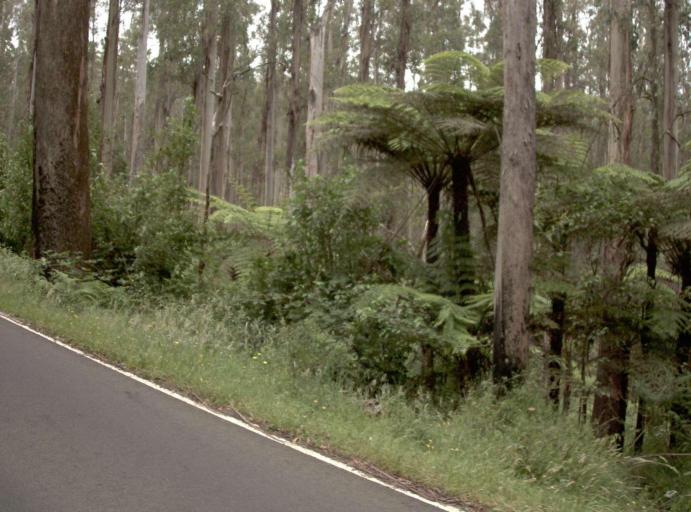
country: AU
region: Victoria
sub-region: Yarra Ranges
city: Healesville
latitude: -37.6066
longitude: 145.6132
